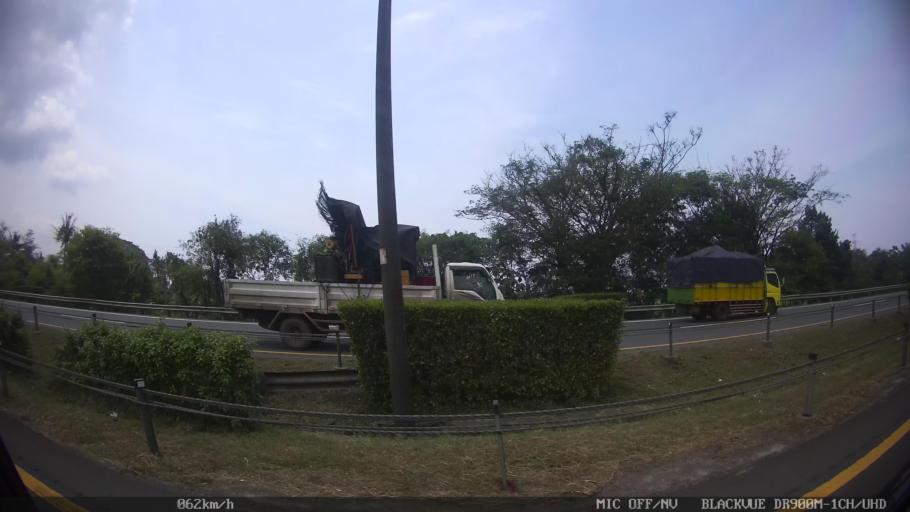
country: ID
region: Banten
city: Bojonegara
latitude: -6.0194
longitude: 106.0899
